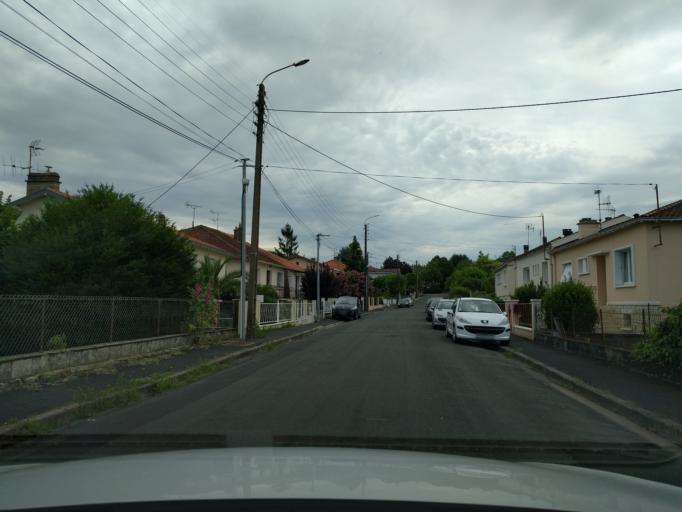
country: FR
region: Poitou-Charentes
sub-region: Departement des Deux-Sevres
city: Niort
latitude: 46.3176
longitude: -0.4421
